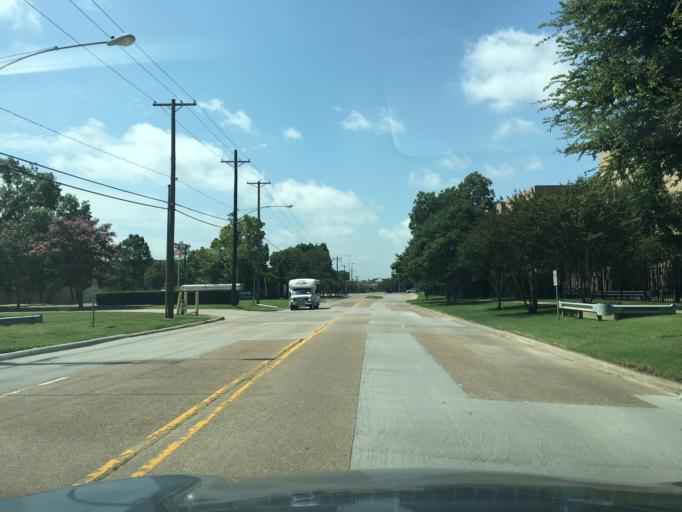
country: US
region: Texas
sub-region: Dallas County
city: Richardson
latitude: 32.9276
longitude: -96.7492
